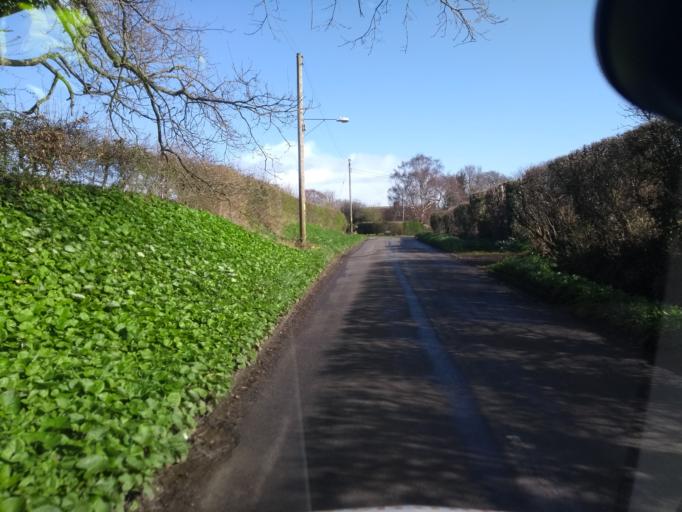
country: GB
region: England
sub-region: Somerset
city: South Petherton
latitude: 50.9669
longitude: -2.8346
